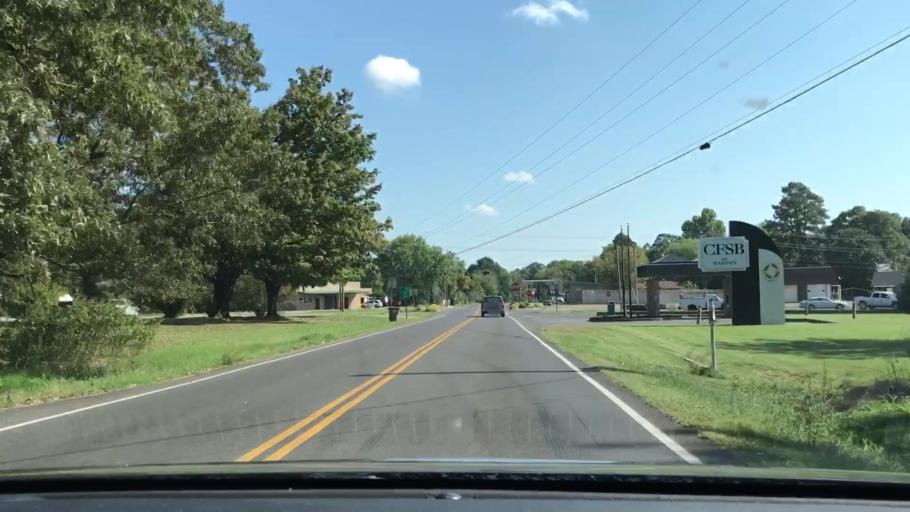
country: US
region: Kentucky
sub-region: Marshall County
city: Benton
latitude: 36.7663
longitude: -88.3052
